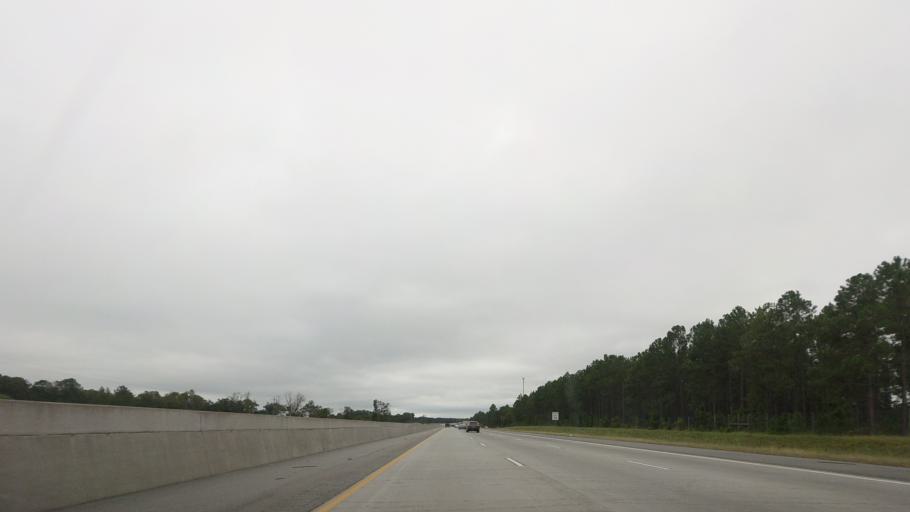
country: US
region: Georgia
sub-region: Tift County
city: Omega
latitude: 31.3248
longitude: -83.4815
